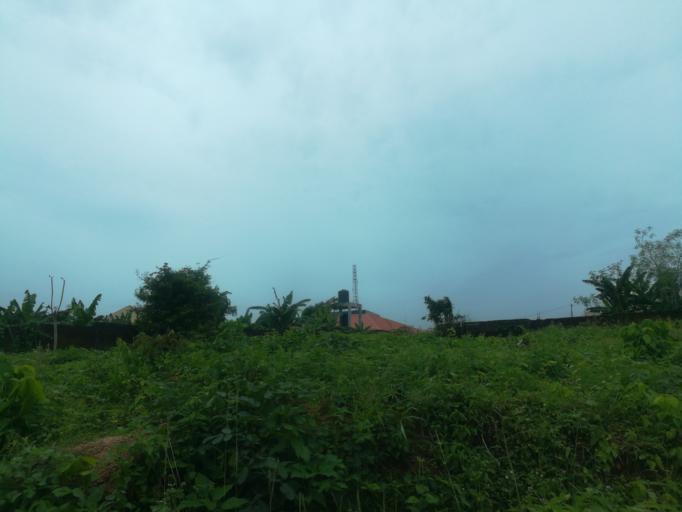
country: NG
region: Oyo
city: Ibadan
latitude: 7.3178
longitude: 3.8844
